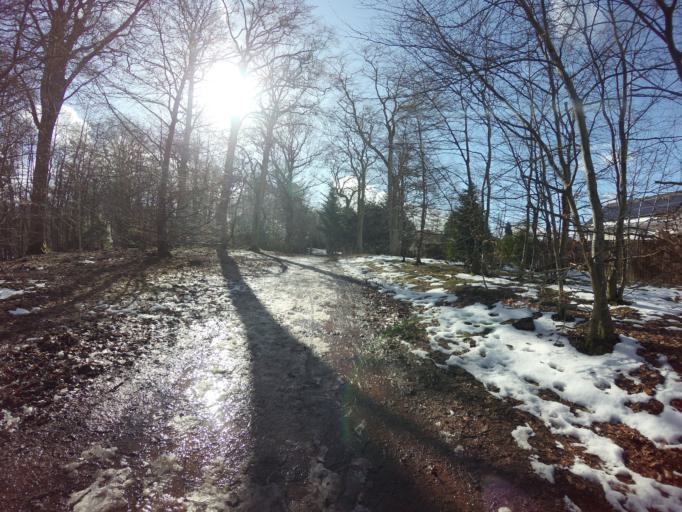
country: GB
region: Scotland
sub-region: West Lothian
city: Mid Calder
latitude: 55.8673
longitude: -3.5061
